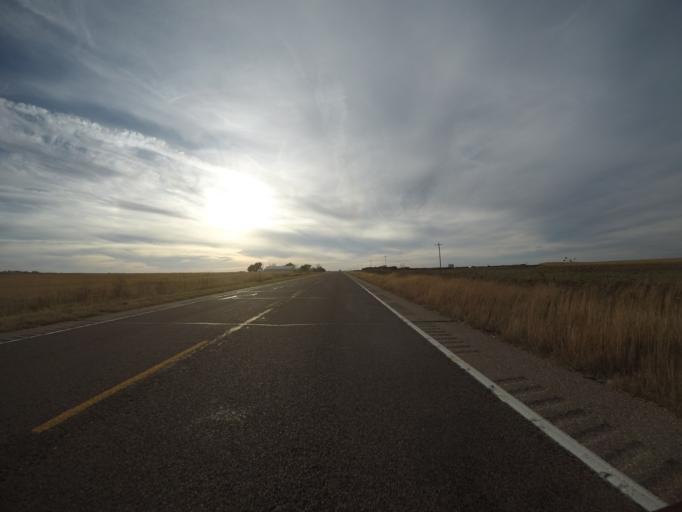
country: US
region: Colorado
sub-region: Kit Carson County
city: Burlington
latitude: 39.6577
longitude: -102.5614
